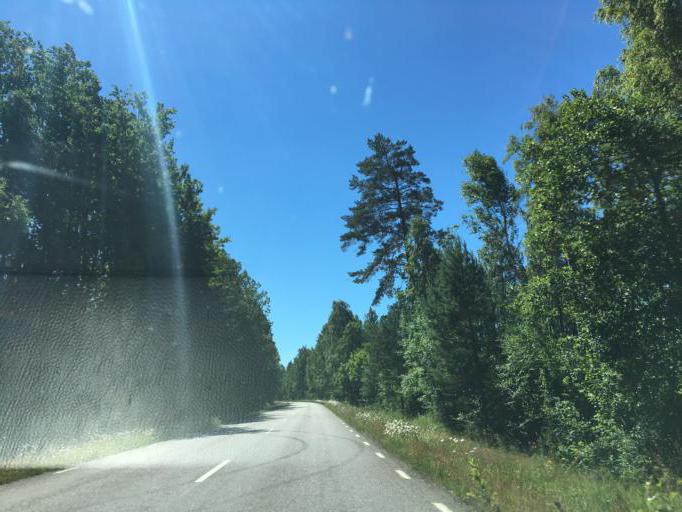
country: SE
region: OErebro
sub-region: Laxa Kommun
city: Laxa
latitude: 58.8272
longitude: 14.5463
